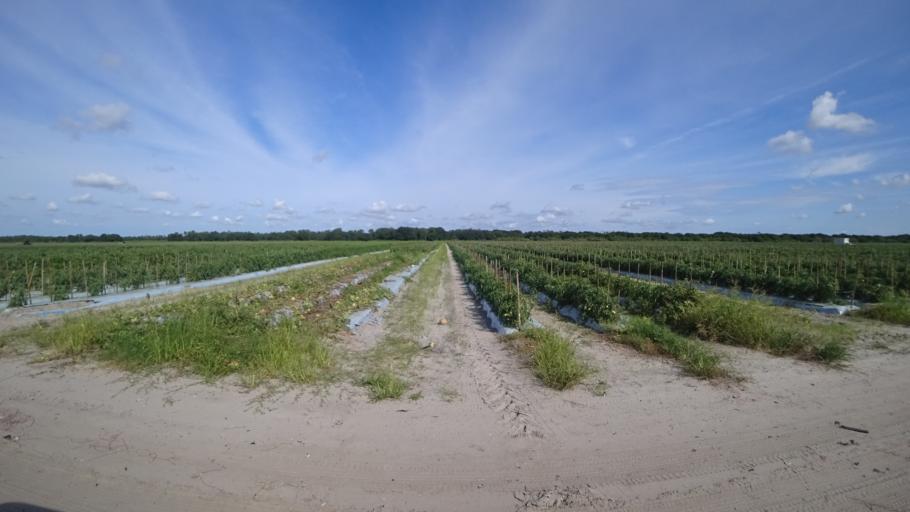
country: US
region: Florida
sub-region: Sarasota County
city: The Meadows
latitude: 27.4483
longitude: -82.3116
